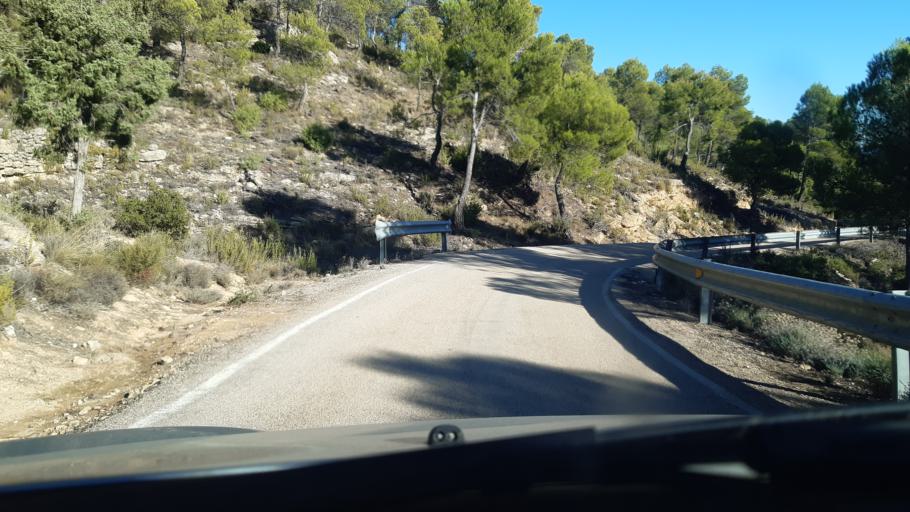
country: ES
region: Aragon
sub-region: Provincia de Teruel
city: Fornoles
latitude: 40.9105
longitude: -0.0167
